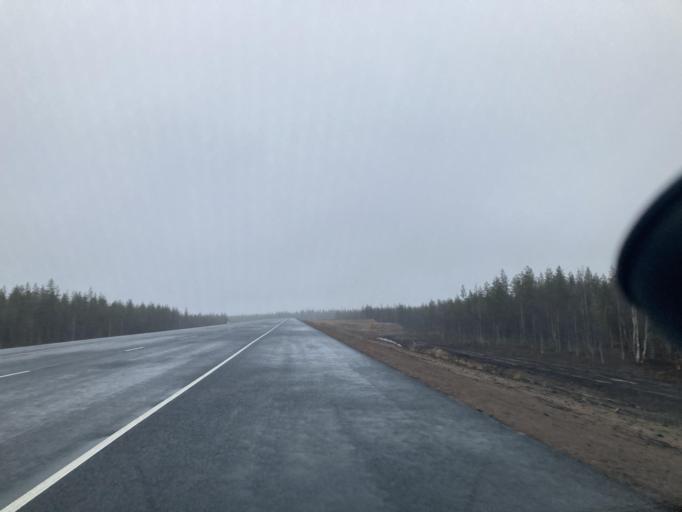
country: FI
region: Lapland
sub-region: Rovaniemi
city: Rovaniemi
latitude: 66.5814
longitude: 25.8004
